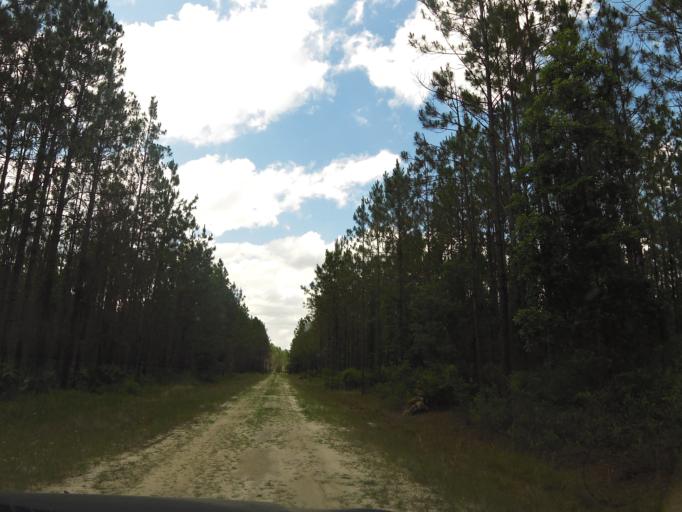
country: US
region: Florida
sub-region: Clay County
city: Keystone Heights
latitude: 29.8582
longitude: -81.8539
